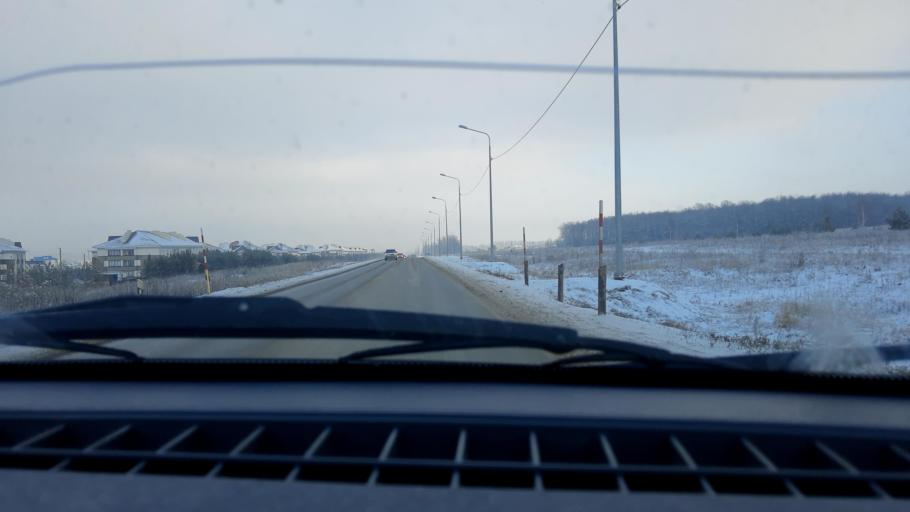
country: RU
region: Bashkortostan
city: Avdon
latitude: 54.4747
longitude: 55.8776
